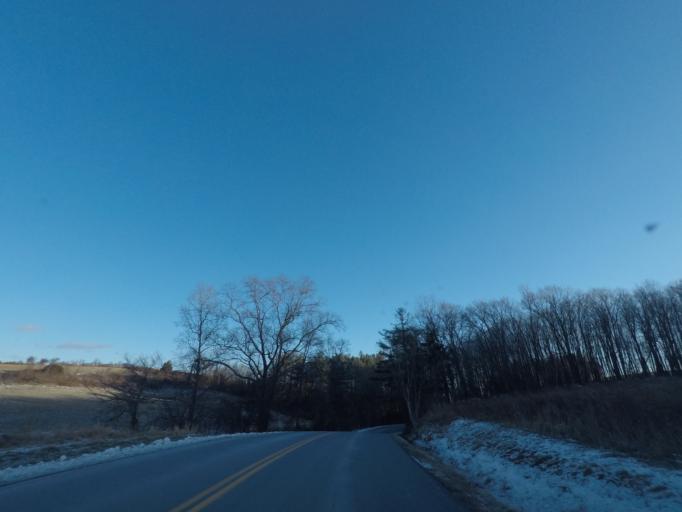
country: US
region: New York
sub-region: Rensselaer County
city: Poestenkill
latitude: 42.7121
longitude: -73.5888
